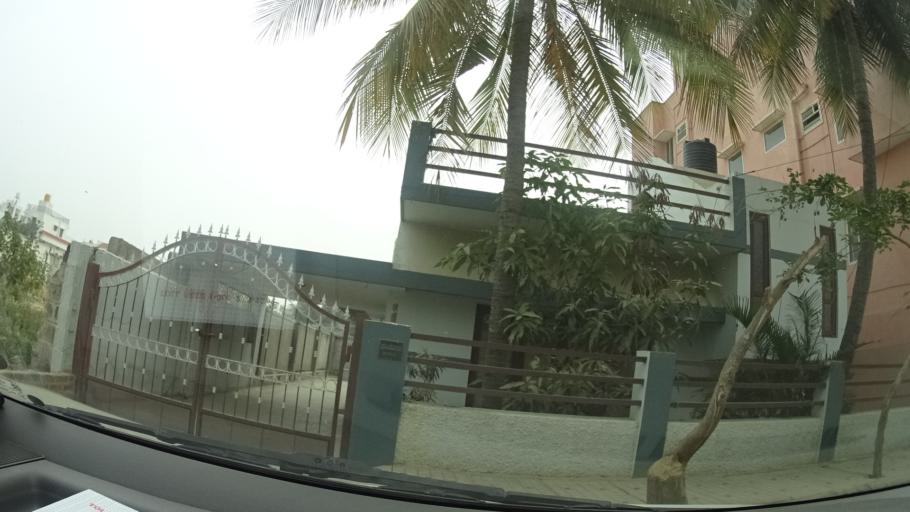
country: IN
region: Karnataka
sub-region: Bangalore Urban
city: Yelahanka
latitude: 13.0404
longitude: 77.6282
